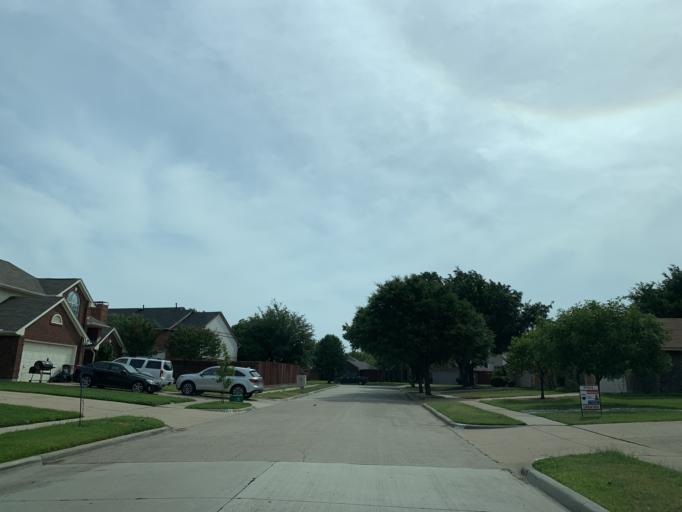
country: US
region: Texas
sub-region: Dallas County
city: Grand Prairie
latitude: 32.6625
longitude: -97.0090
